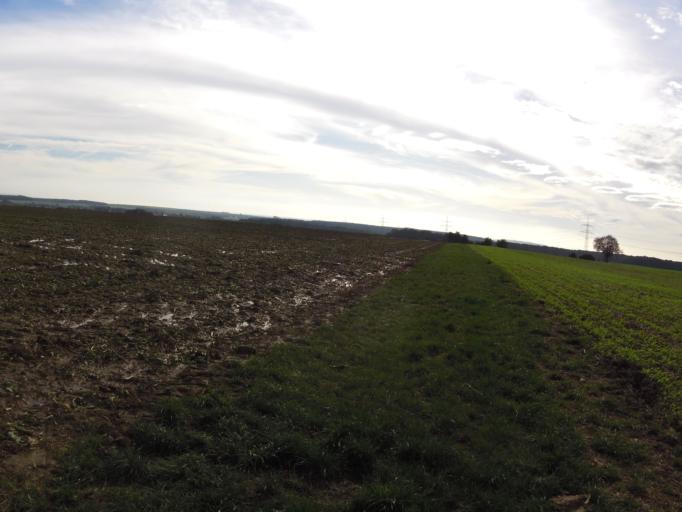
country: DE
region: Bavaria
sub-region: Regierungsbezirk Unterfranken
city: Sommerhausen
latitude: 49.7177
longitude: 10.0656
